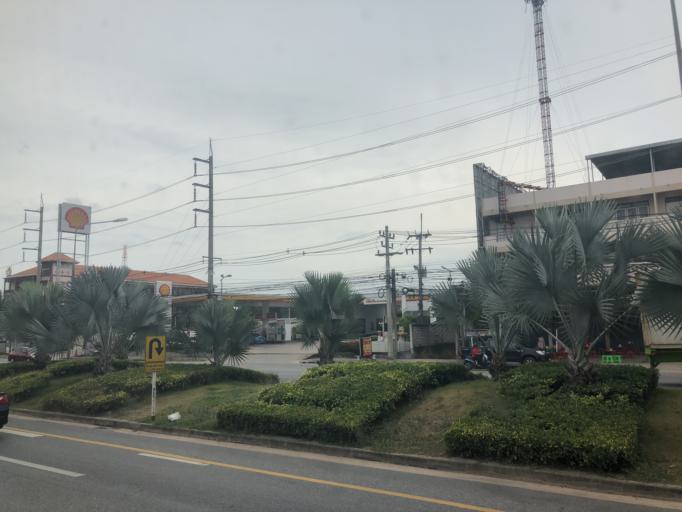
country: TH
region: Chon Buri
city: Bang Lamung
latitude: 13.0231
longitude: 100.9313
